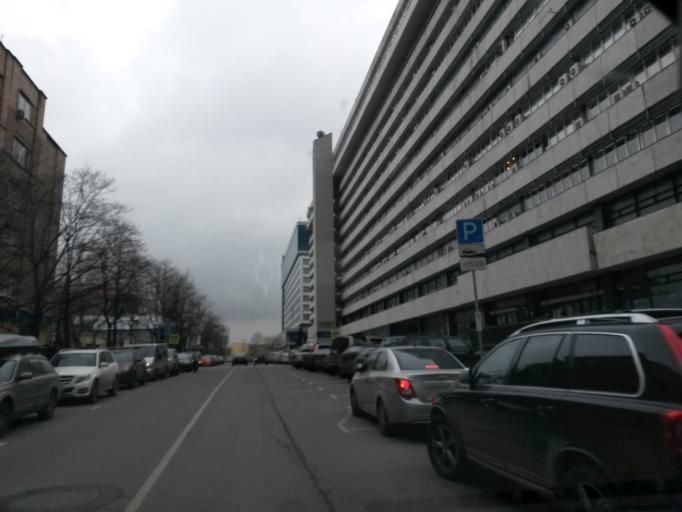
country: RU
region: Moscow
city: Mar'ina Roshcha
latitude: 55.7887
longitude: 37.5819
